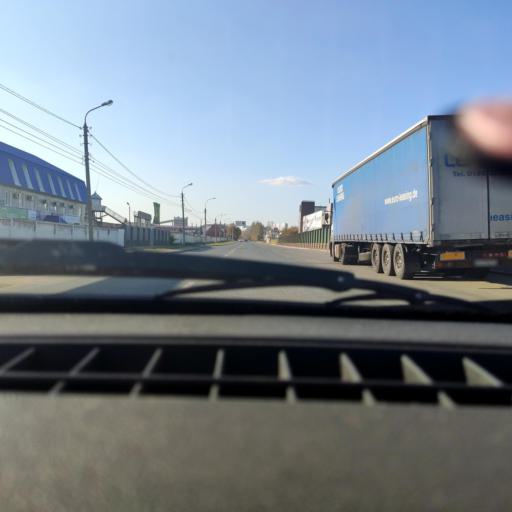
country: RU
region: Bashkortostan
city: Ufa
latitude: 54.8044
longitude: 56.0944
